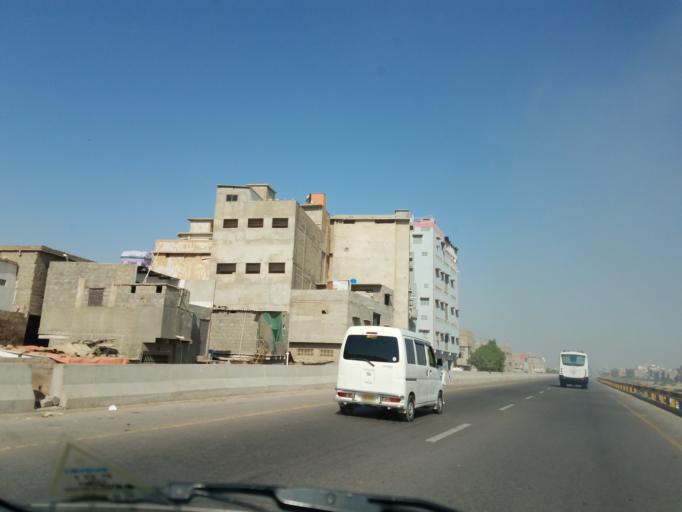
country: PK
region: Sindh
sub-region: Karachi District
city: Karachi
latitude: 24.9122
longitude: 67.0708
